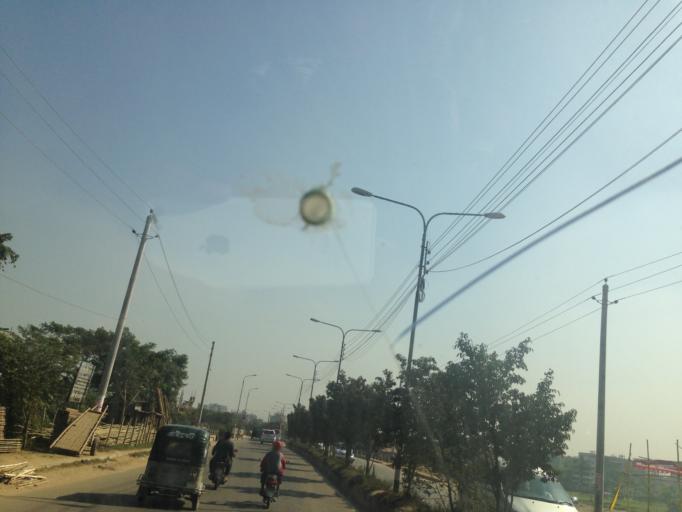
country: BD
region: Dhaka
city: Tungi
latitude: 23.8220
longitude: 90.3827
